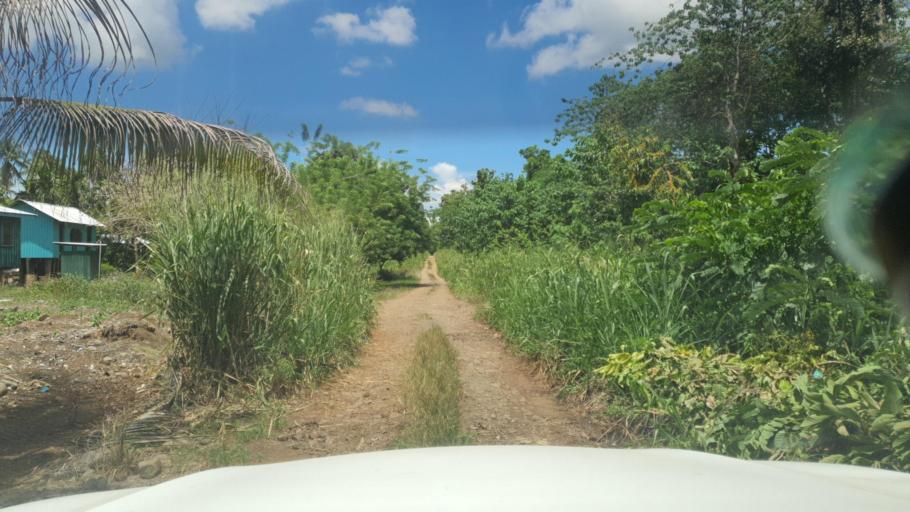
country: SB
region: Guadalcanal
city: Honiara
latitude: -9.5198
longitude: 160.2494
